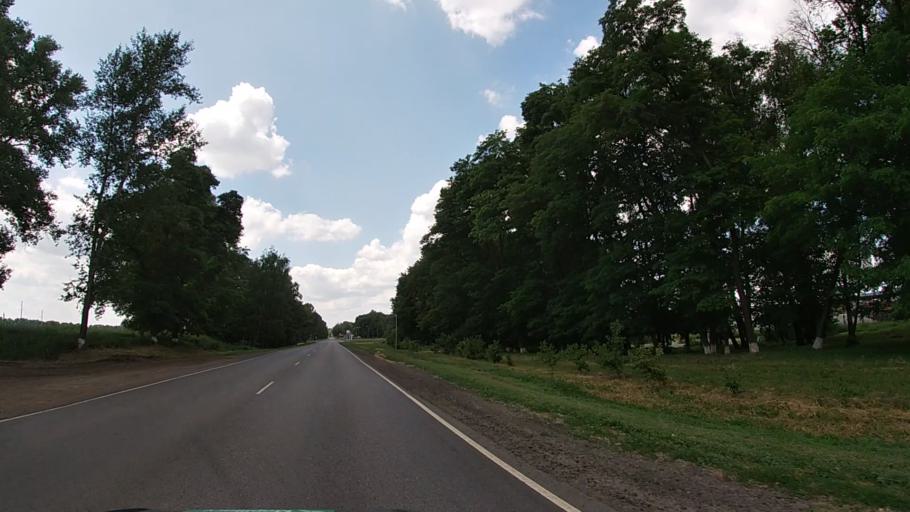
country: RU
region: Belgorod
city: Grayvoron
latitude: 50.4945
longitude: 35.7088
